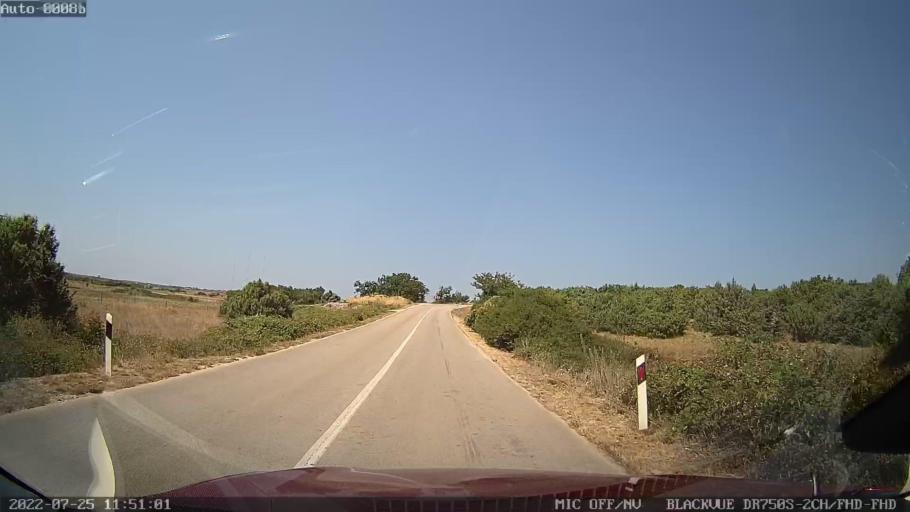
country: HR
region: Zadarska
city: Vrsi
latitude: 44.2376
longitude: 15.2566
